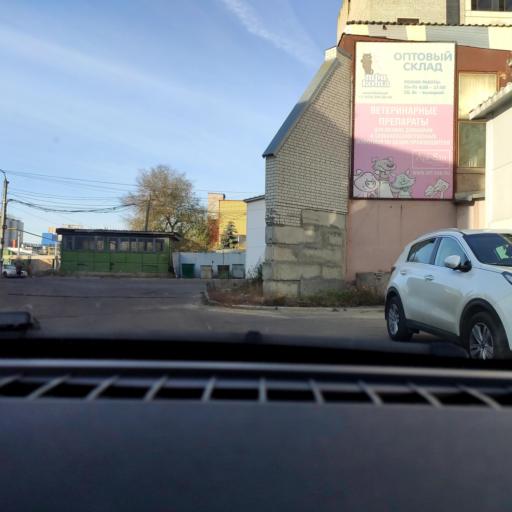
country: RU
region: Voronezj
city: Somovo
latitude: 51.6708
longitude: 39.2979
